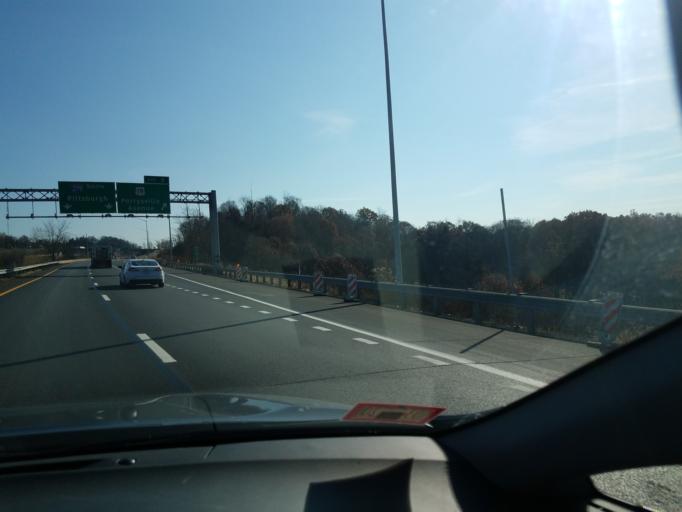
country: US
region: Pennsylvania
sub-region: Allegheny County
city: West View
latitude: 40.5058
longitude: -80.0321
